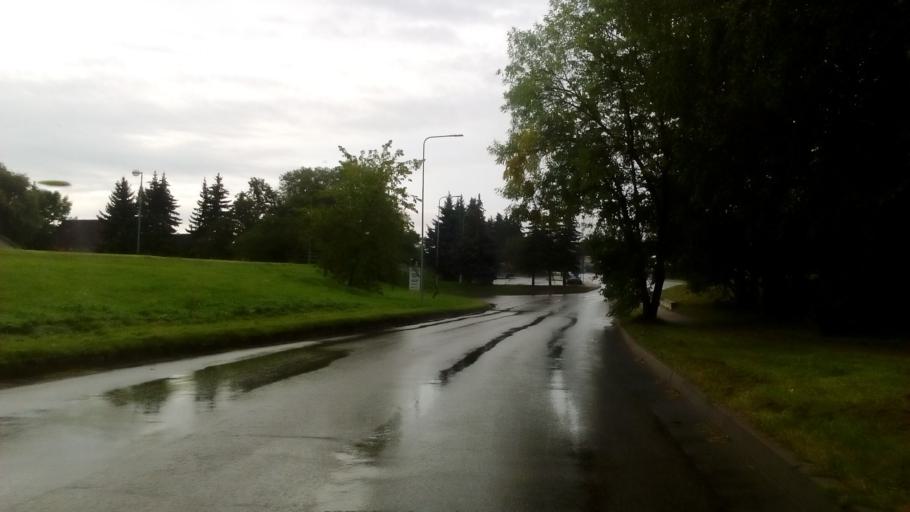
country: LT
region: Alytaus apskritis
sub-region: Alytus
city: Alytus
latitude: 54.3932
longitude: 24.0362
